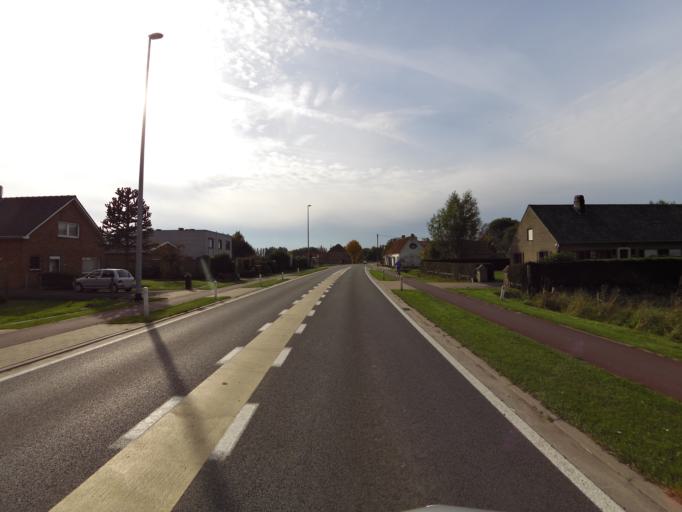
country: BE
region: Flanders
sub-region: Provincie West-Vlaanderen
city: Oudenburg
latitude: 51.1595
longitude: 2.9991
